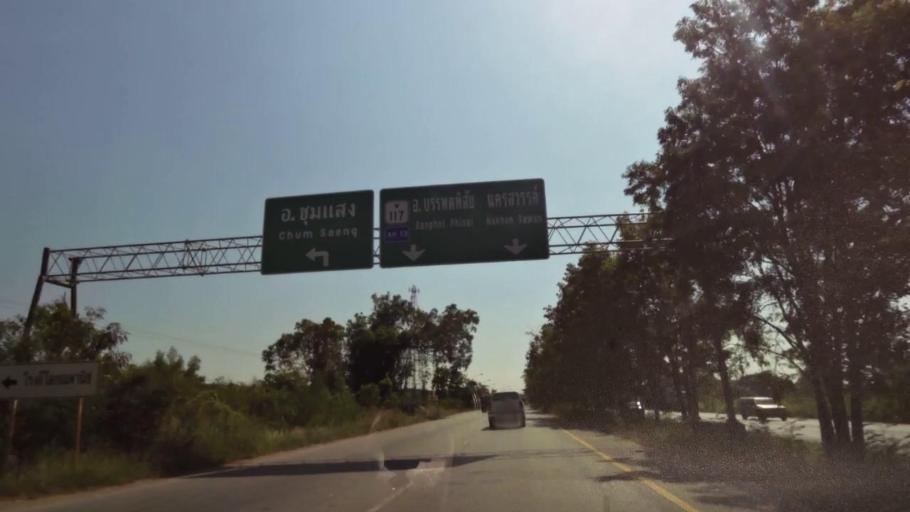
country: TH
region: Nakhon Sawan
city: Kao Liao
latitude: 15.8724
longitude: 100.1164
